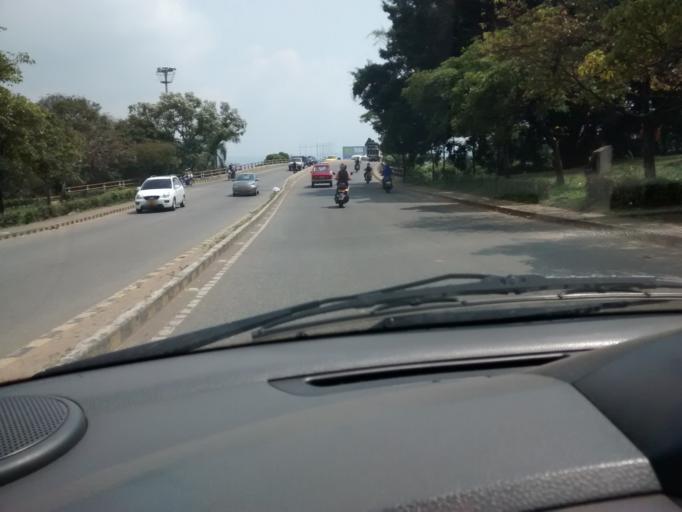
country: CO
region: Santander
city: Bucaramanga
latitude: 7.1069
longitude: -73.1139
